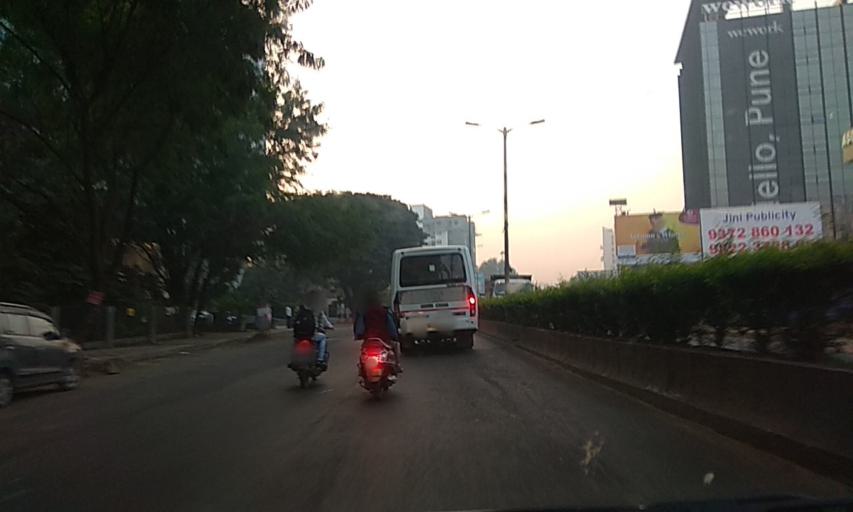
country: IN
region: Maharashtra
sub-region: Pune Division
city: Pune
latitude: 18.5212
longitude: 73.9322
